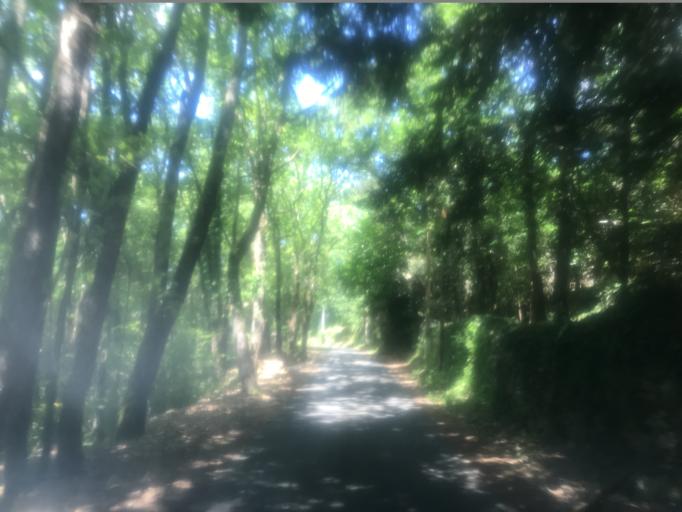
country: FR
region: Aquitaine
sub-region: Departement de la Dordogne
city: Cenac-et-Saint-Julien
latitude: 44.8229
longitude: 1.1935
